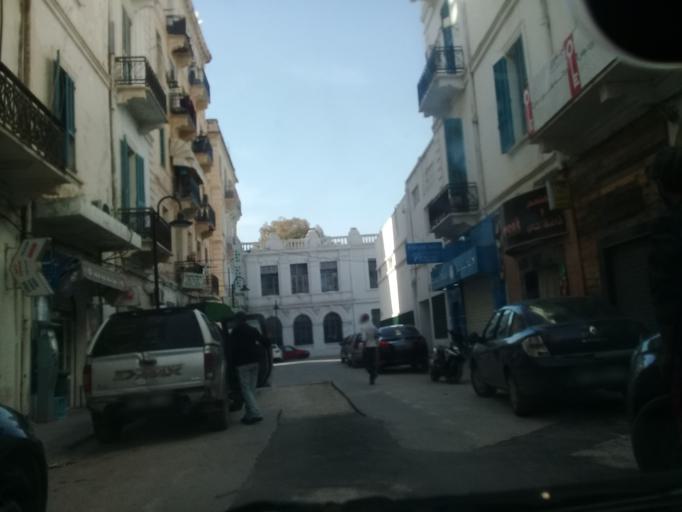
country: TN
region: Tunis
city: Tunis
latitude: 36.8012
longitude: 10.1802
